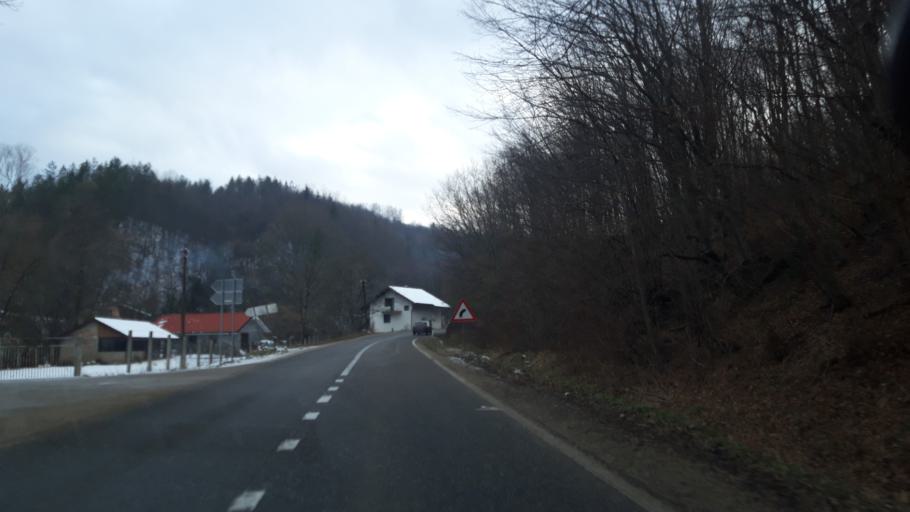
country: BA
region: Republika Srpska
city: Milici
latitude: 44.1709
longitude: 19.0162
